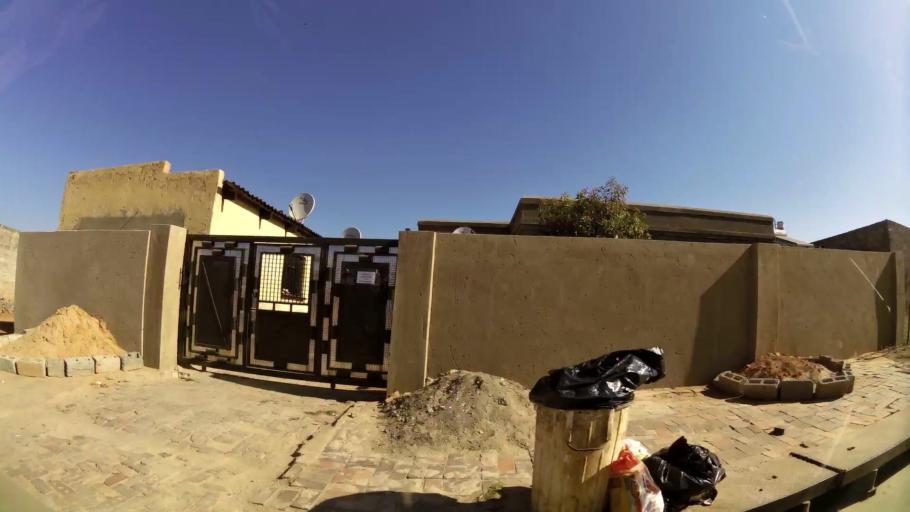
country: ZA
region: Gauteng
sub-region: Ekurhuleni Metropolitan Municipality
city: Tembisa
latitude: -26.0264
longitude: 28.2379
